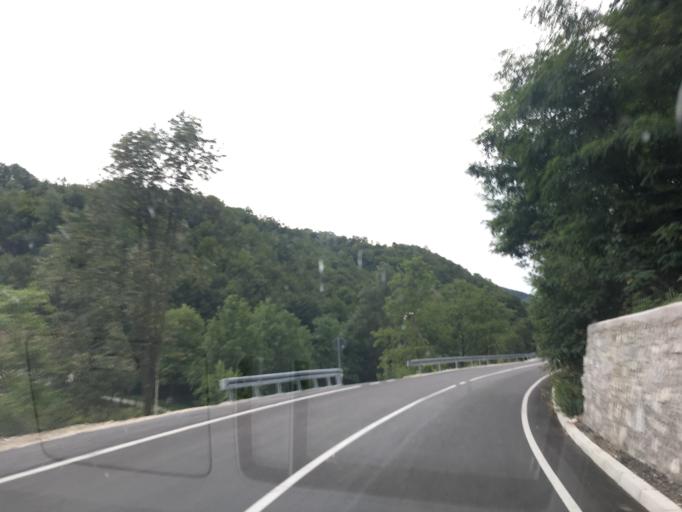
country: RS
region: Central Serbia
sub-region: Moravicki Okrug
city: Gornji Milanovac
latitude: 44.1586
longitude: 20.5081
